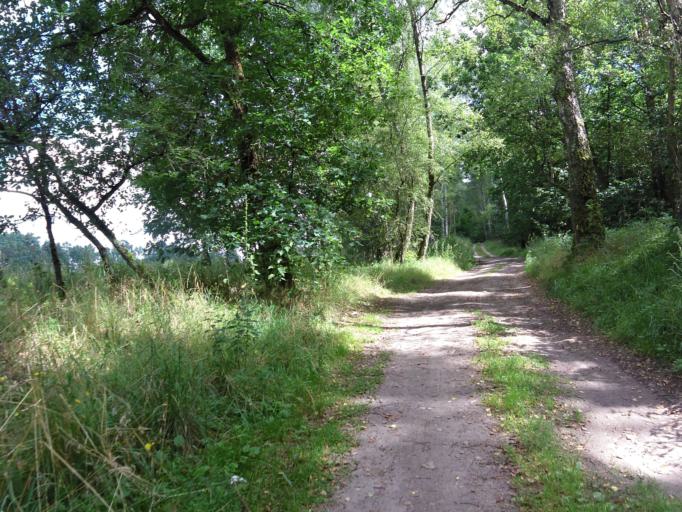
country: DE
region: Brandenburg
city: Lychen
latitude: 53.2405
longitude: 13.3591
